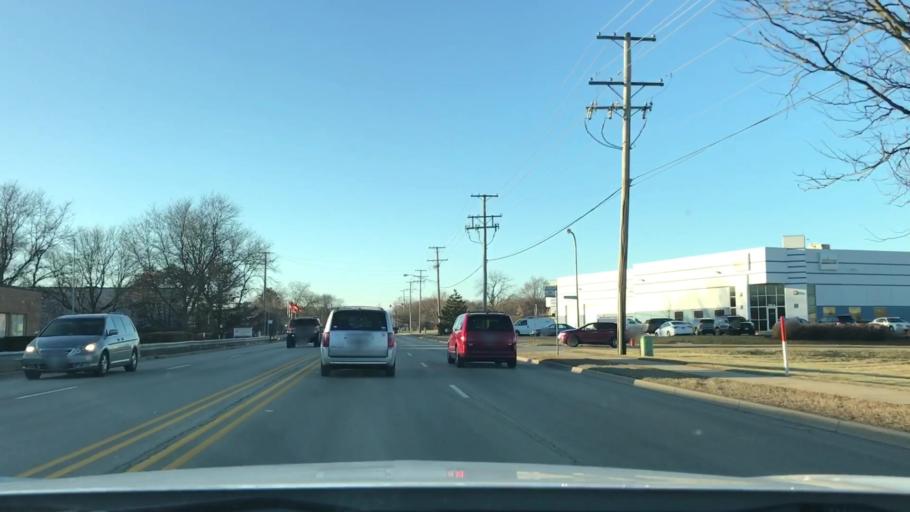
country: US
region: Illinois
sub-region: Kane County
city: Sleepy Hollow
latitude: 42.0588
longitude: -88.3222
